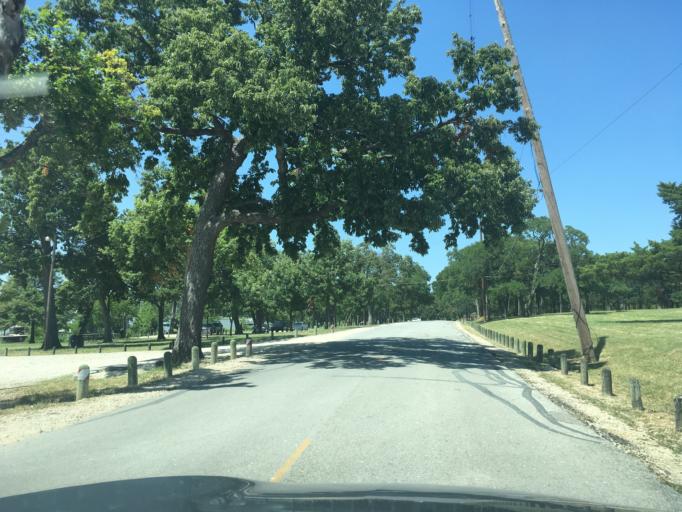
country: US
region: Texas
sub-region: Dallas County
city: Highland Park
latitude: 32.8436
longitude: -96.7183
